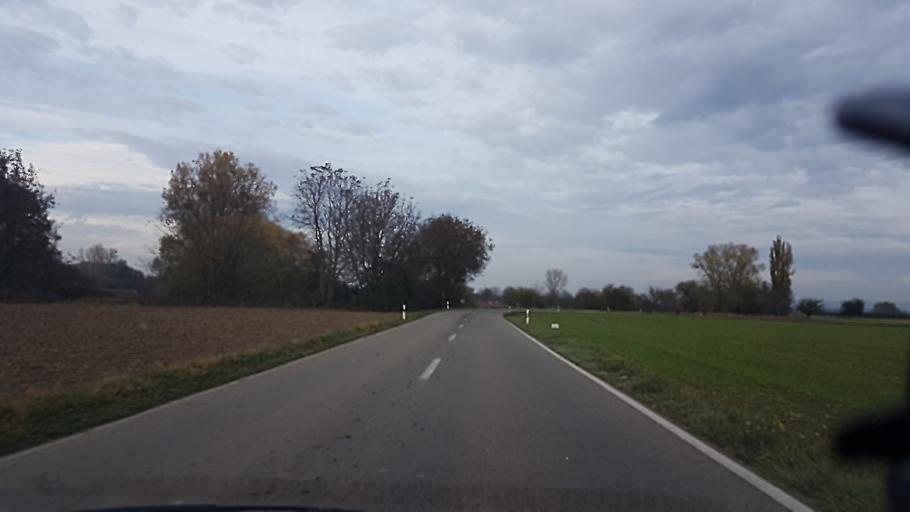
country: DE
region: Baden-Wuerttemberg
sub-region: Freiburg Region
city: Wyhl
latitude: 48.1753
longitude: 7.6581
